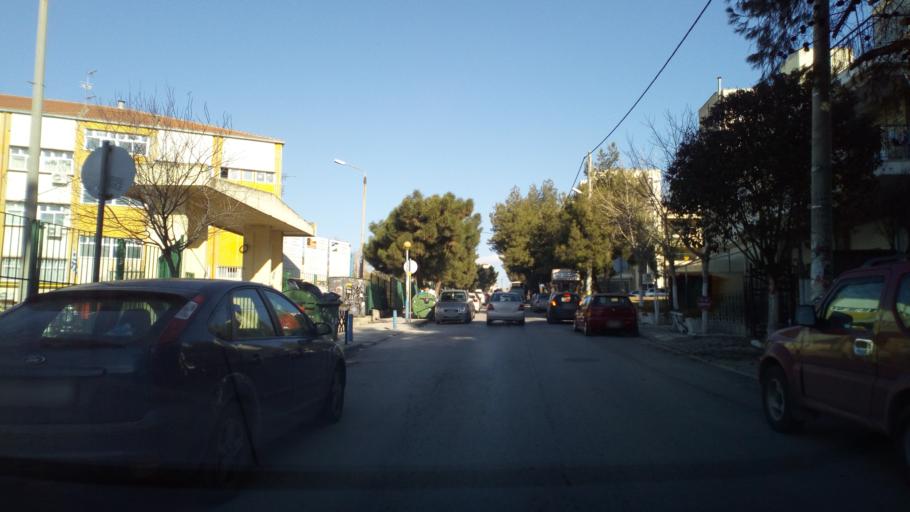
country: GR
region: Central Macedonia
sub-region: Nomos Thessalonikis
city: Evosmos
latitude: 40.6751
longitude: 22.9108
